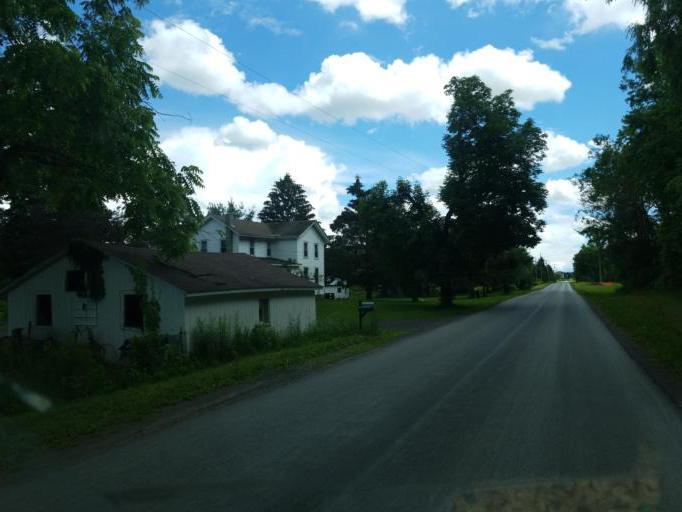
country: US
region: New York
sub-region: Wayne County
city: Clyde
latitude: 43.0485
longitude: -76.8840
